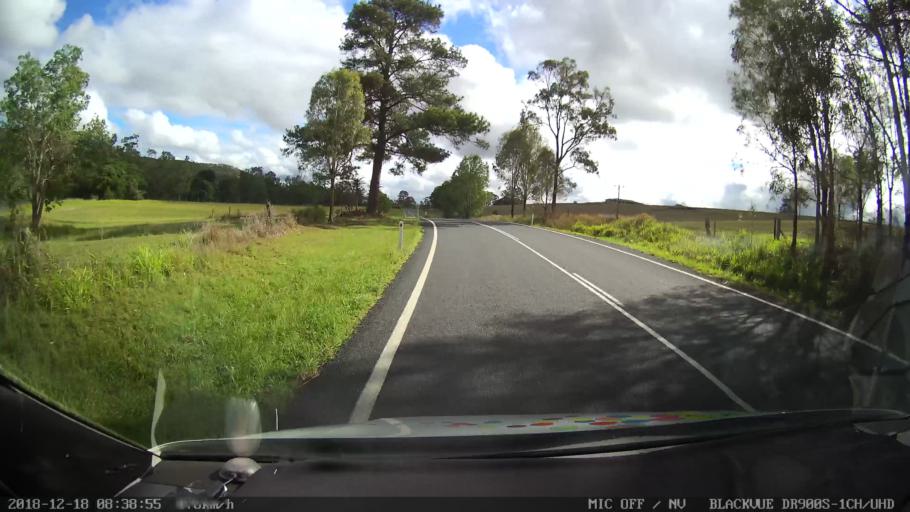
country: AU
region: New South Wales
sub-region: Kyogle
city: Kyogle
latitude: -28.2526
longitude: 152.8328
